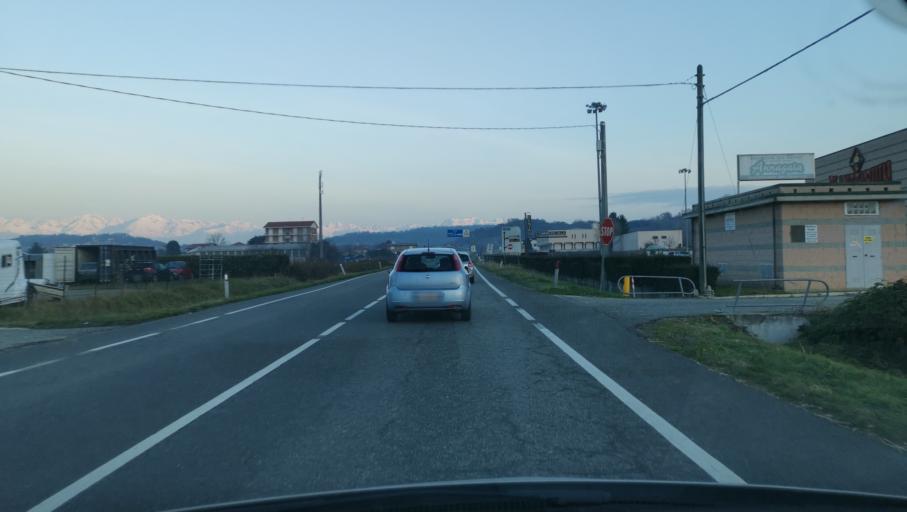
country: IT
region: Piedmont
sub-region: Provincia di Torino
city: Caluso
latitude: 45.3050
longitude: 7.8787
